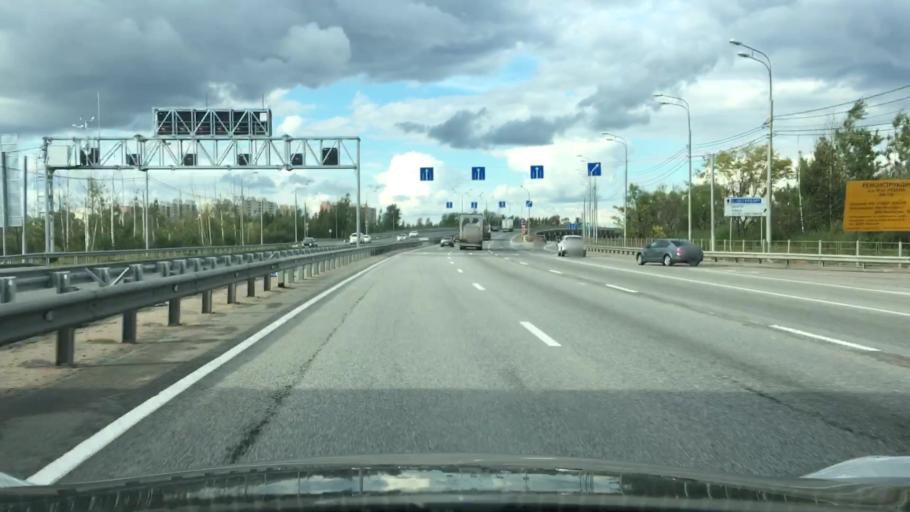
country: RU
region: Tverskaya
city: Tver
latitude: 56.8381
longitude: 35.7948
